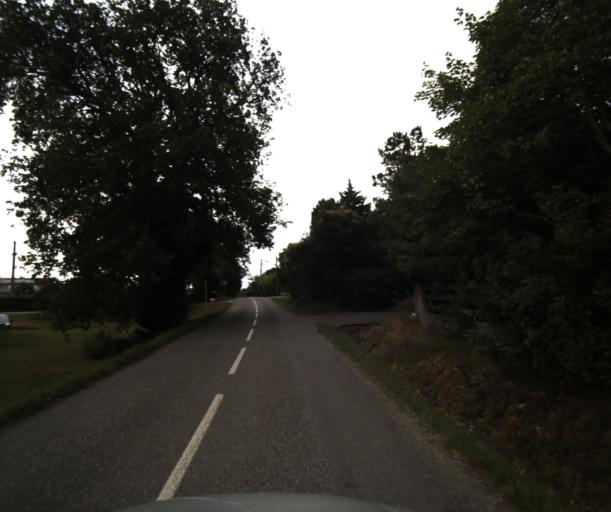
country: FR
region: Midi-Pyrenees
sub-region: Departement de la Haute-Garonne
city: Le Fauga
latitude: 43.4137
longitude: 1.3132
